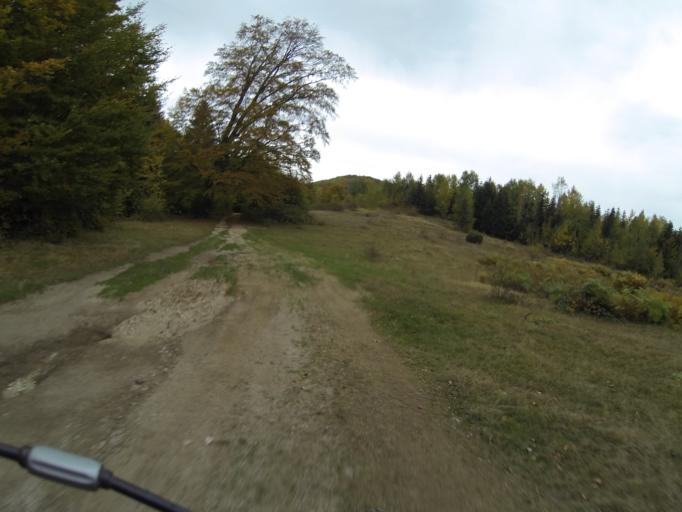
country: RO
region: Gorj
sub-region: Comuna Tismana
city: Sohodol
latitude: 45.1279
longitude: 22.8830
